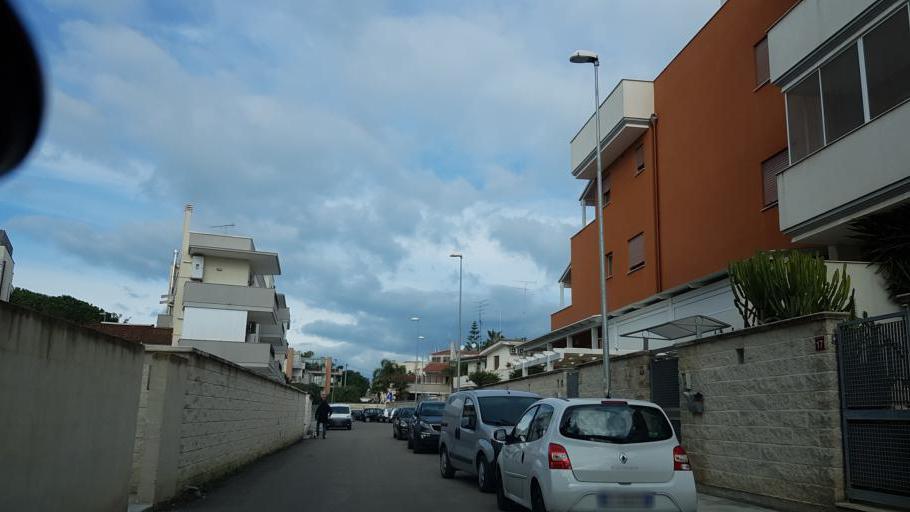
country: IT
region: Apulia
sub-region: Provincia di Brindisi
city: Materdomini
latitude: 40.6561
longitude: 17.9584
